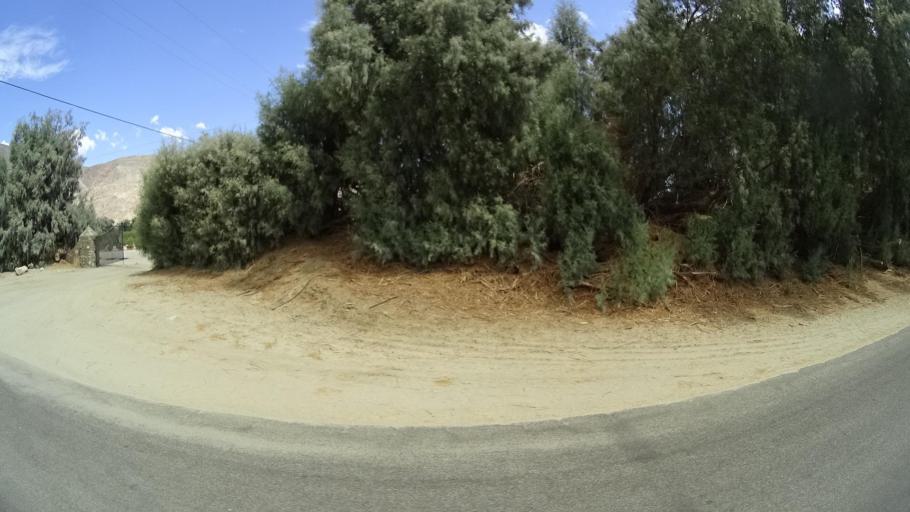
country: US
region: California
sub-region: San Diego County
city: Borrego Springs
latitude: 33.3081
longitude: -116.3500
